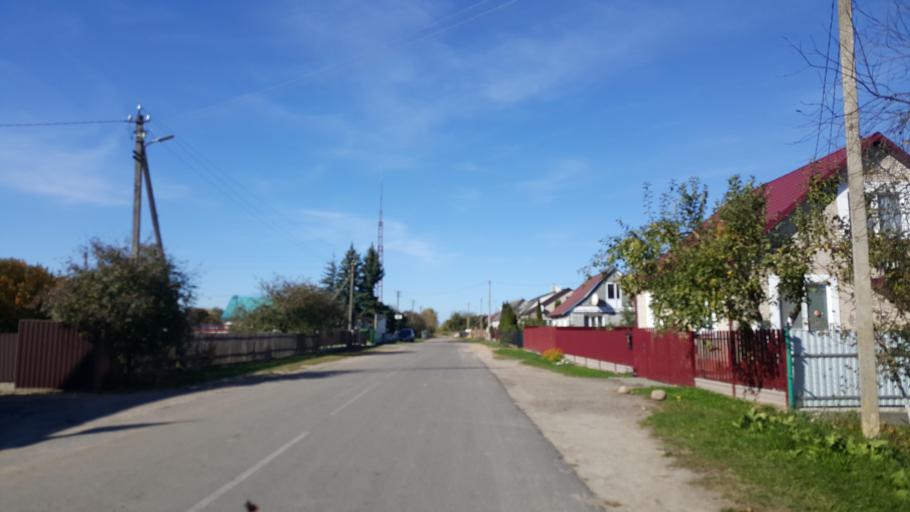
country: BY
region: Brest
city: Kamyanyets
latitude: 52.4014
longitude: 23.7926
